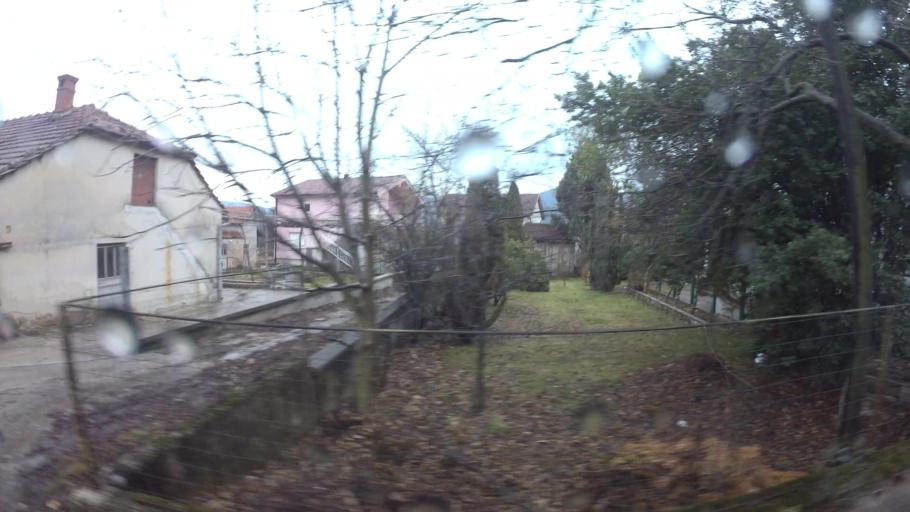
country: BA
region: Federation of Bosnia and Herzegovina
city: Cim
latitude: 43.3530
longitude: 17.7833
